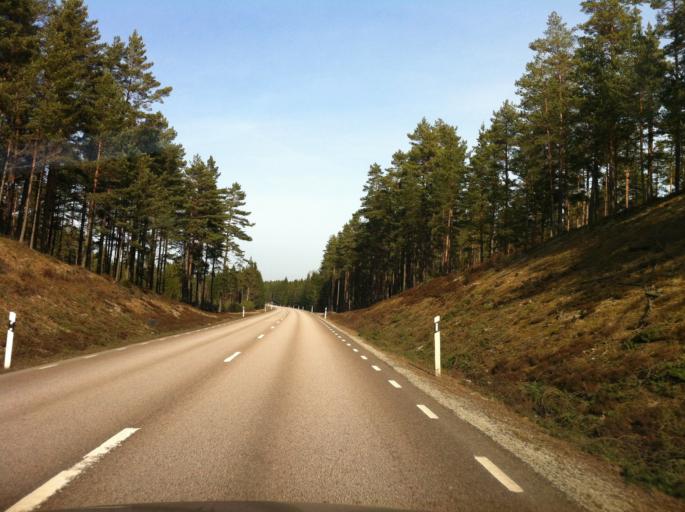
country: SE
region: Joenkoeping
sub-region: Mullsjo Kommun
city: Mullsjoe
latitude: 58.0548
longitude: 13.8546
